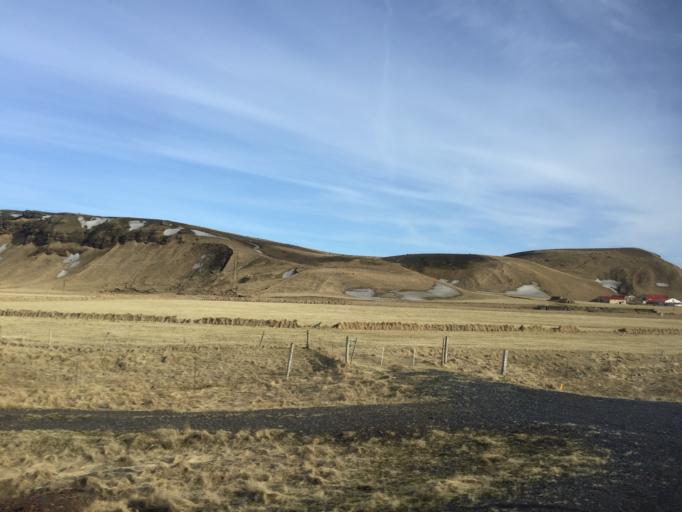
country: IS
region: South
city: Vestmannaeyjar
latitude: 63.4409
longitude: -19.1976
